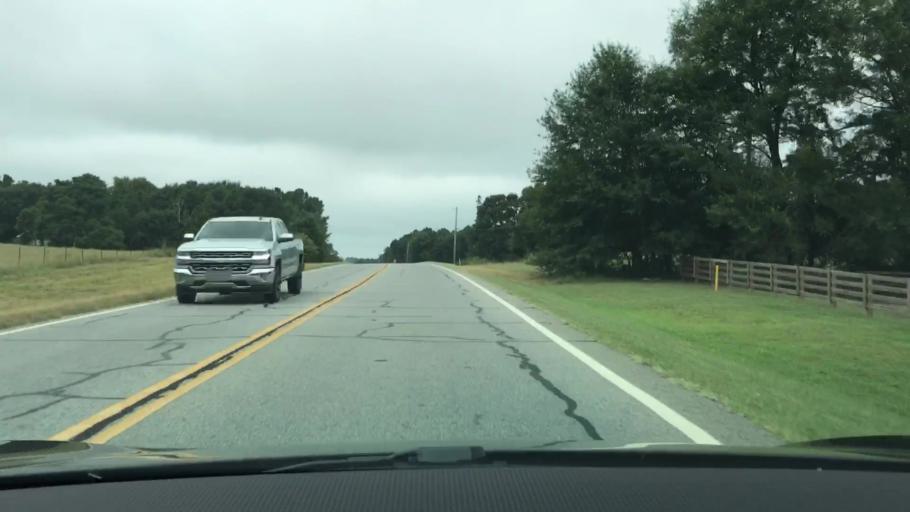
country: US
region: Georgia
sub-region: Oconee County
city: Watkinsville
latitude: 33.8434
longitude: -83.3882
